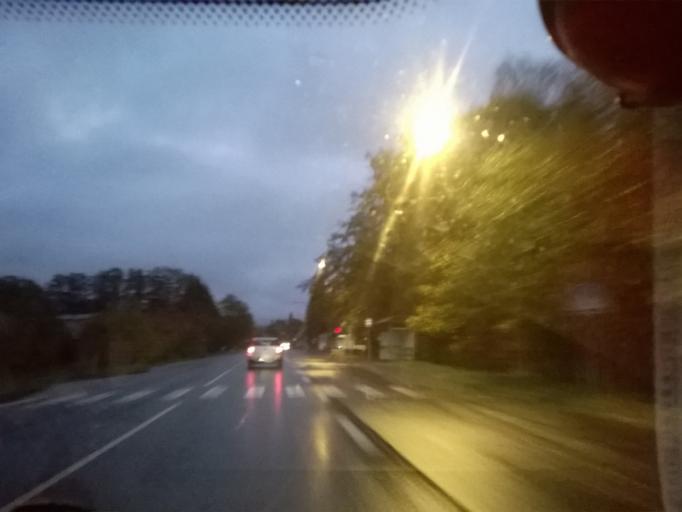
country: EE
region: Harju
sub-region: Viimsi vald
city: Haabneeme
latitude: 59.5163
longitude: 24.8143
